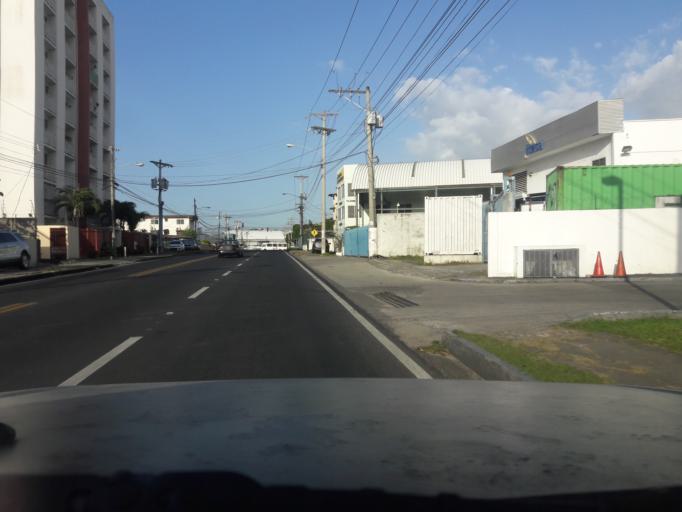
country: PA
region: Panama
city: Panama
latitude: 9.0212
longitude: -79.4988
